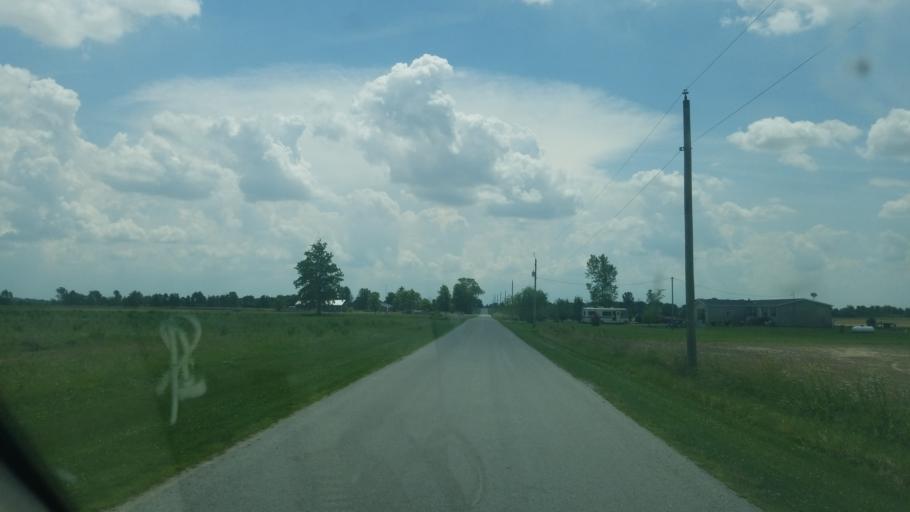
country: US
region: Ohio
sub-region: Hardin County
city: Forest
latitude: 40.7981
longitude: -83.6050
